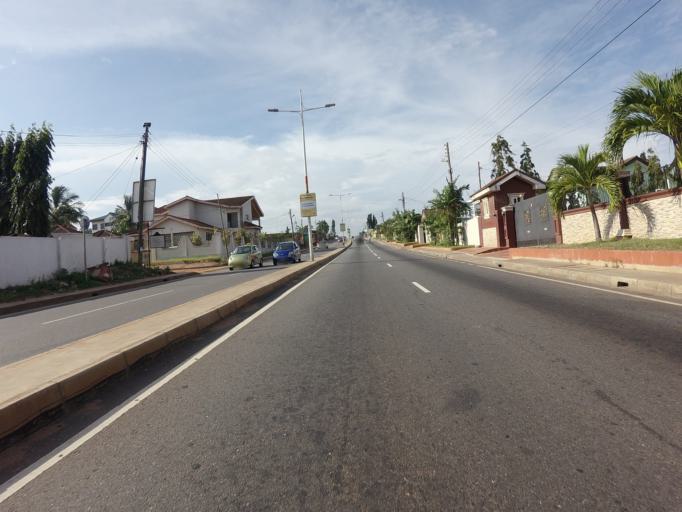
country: GH
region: Greater Accra
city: Medina Estates
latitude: 5.6219
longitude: -0.1528
